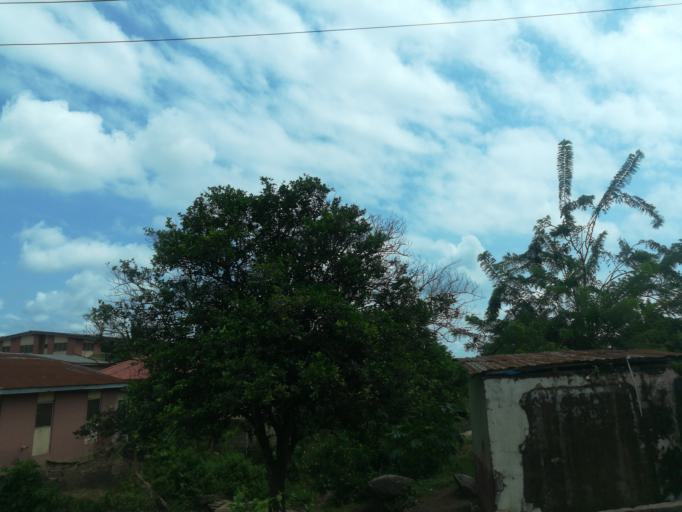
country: NG
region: Oyo
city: Egbeda
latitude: 7.4205
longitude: 3.9990
